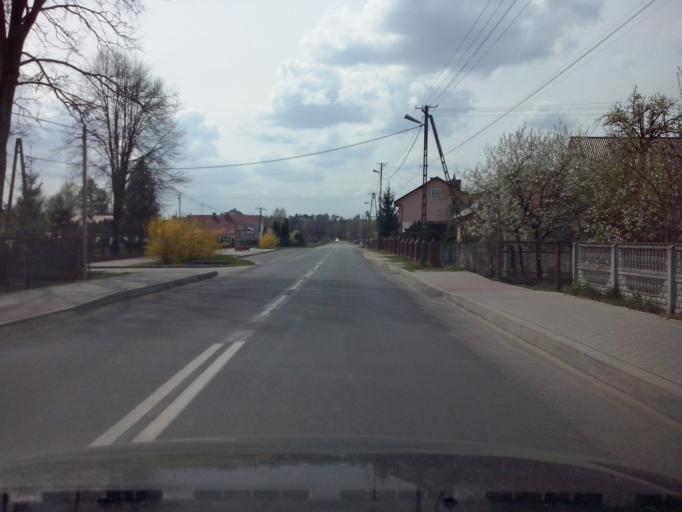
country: PL
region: Subcarpathian Voivodeship
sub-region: Powiat lezajski
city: Letownia
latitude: 50.3682
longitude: 22.2159
